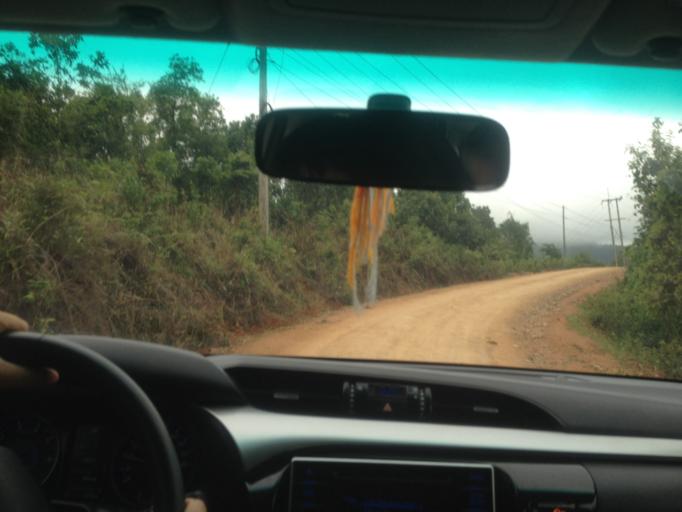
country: TH
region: Nan
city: Chaloem Phra Kiat
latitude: 19.9950
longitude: 101.1345
